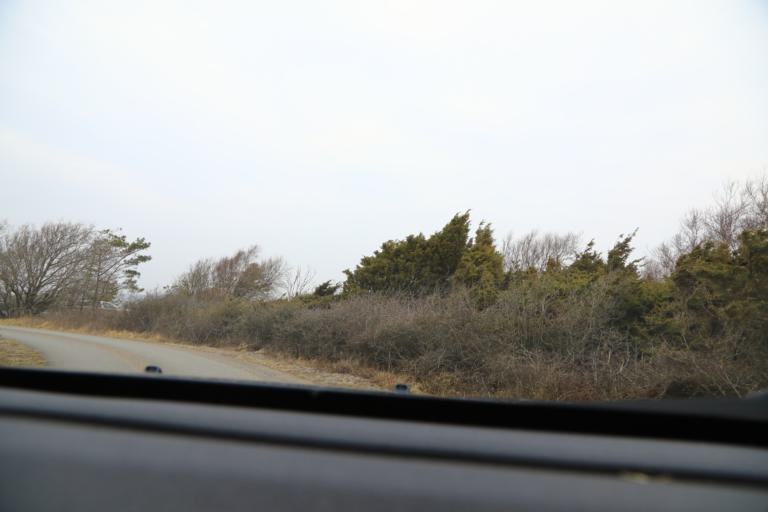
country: SE
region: Halland
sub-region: Kungsbacka Kommun
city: Frillesas
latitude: 57.2672
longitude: 12.1094
